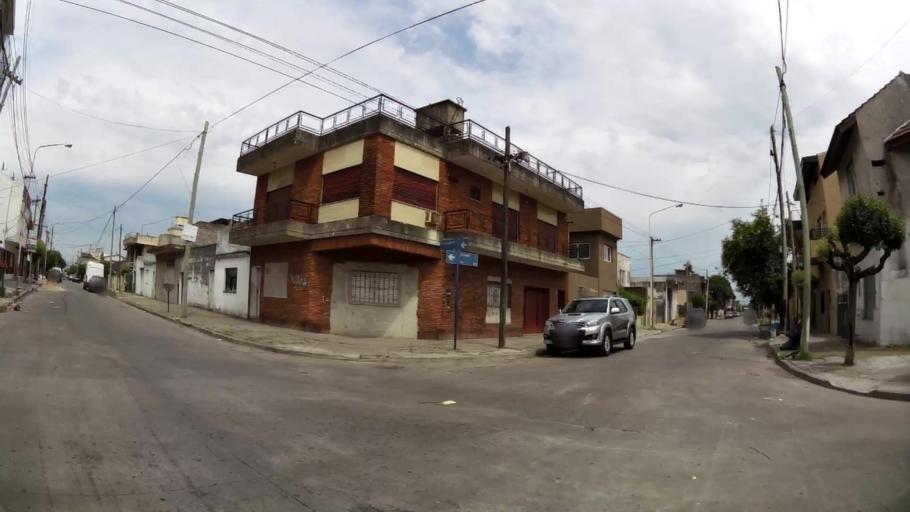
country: AR
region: Buenos Aires F.D.
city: Villa Lugano
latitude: -34.6870
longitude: -58.5039
